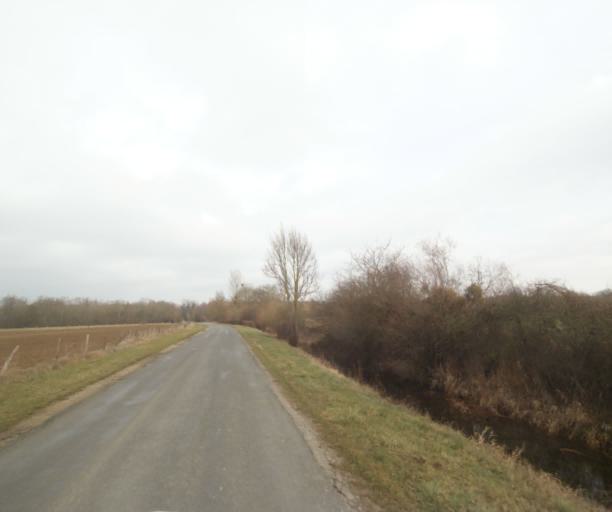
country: FR
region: Champagne-Ardenne
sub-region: Departement de la Haute-Marne
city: Villiers-en-Lieu
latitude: 48.6613
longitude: 4.8306
